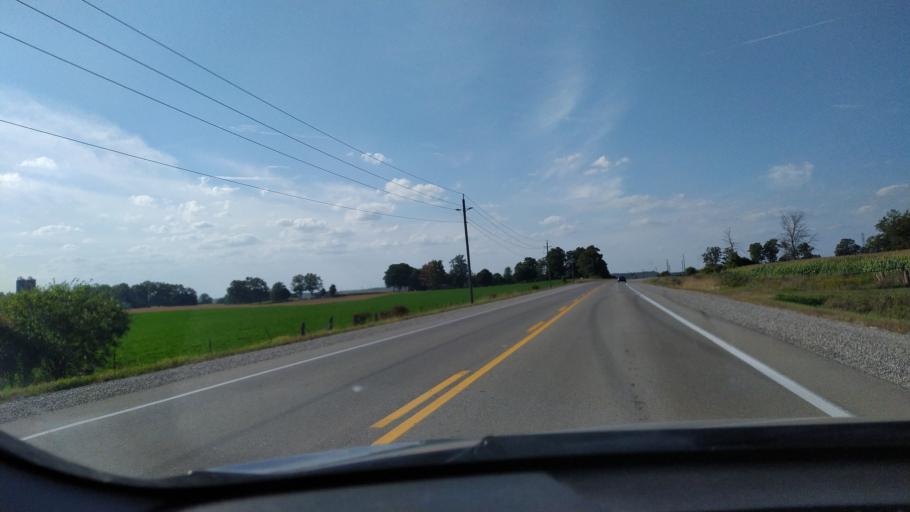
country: CA
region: Ontario
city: Ingersoll
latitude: 43.0607
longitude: -80.8349
